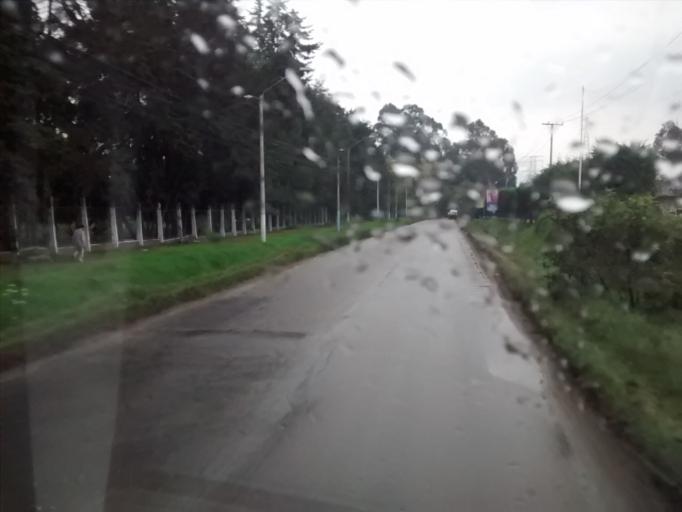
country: CO
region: Cundinamarca
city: Cota
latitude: 4.7679
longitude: -74.0805
